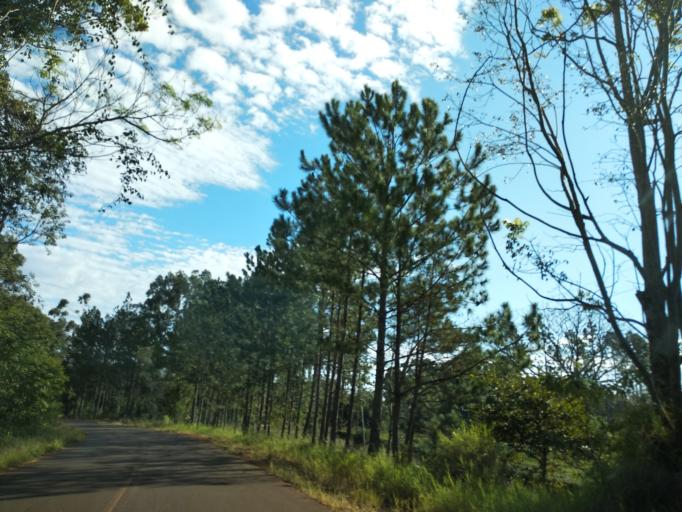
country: AR
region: Misiones
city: Aristobulo del Valle
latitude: -27.0704
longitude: -54.8282
